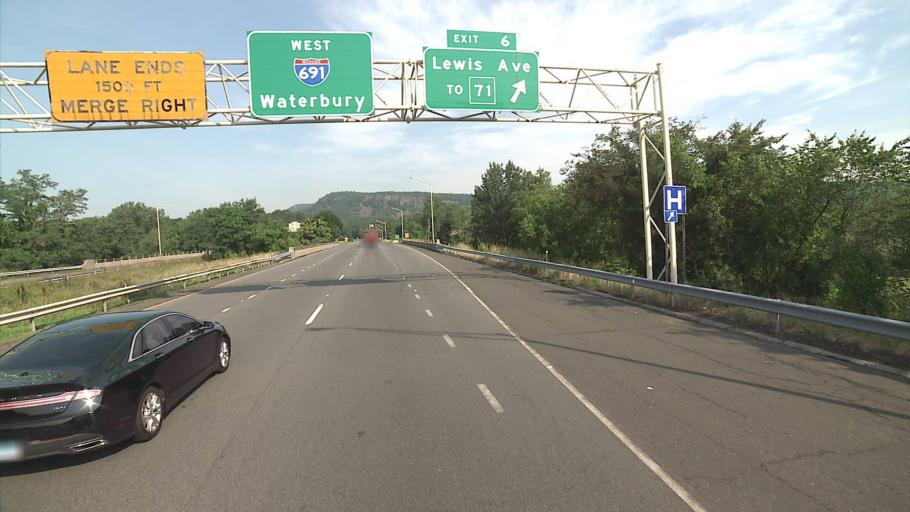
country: US
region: Connecticut
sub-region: New Haven County
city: Meriden
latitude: 41.5470
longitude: -72.8039
